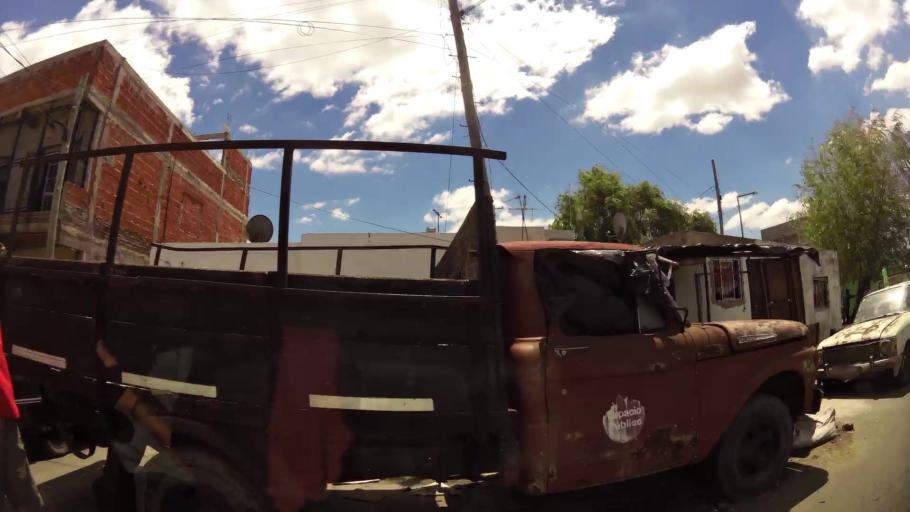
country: AR
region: Buenos Aires
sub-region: Partido de Lanus
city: Lanus
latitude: -34.7174
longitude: -58.4254
